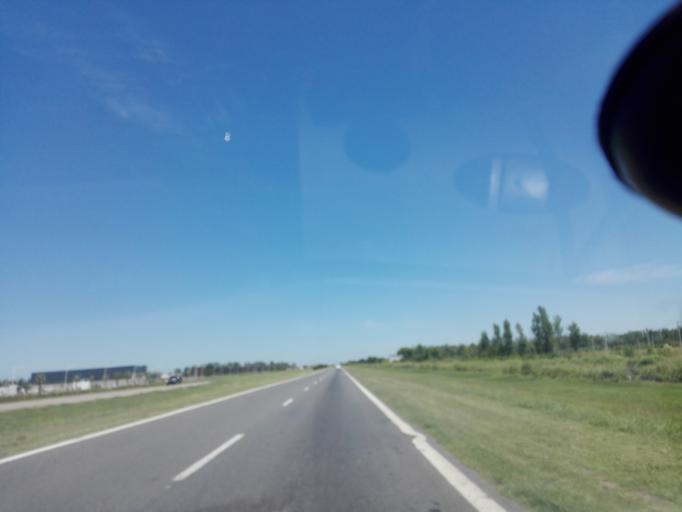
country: AR
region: Santa Fe
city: Roldan
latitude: -32.9299
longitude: -60.8745
